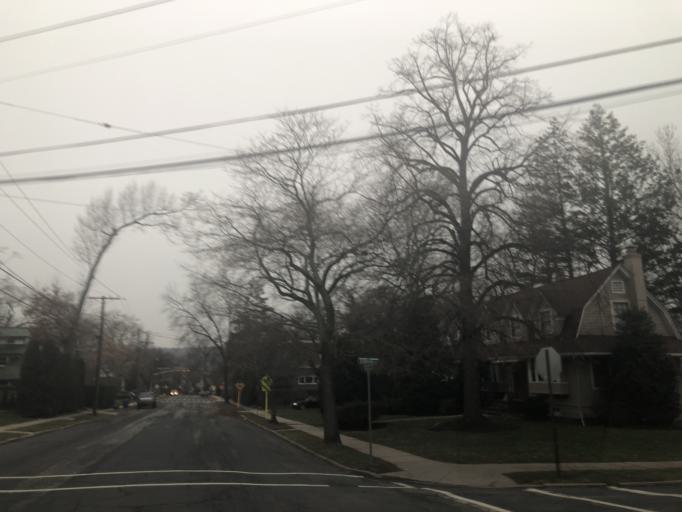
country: US
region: New Jersey
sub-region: Essex County
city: Maplewood
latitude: 40.7234
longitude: -74.2697
